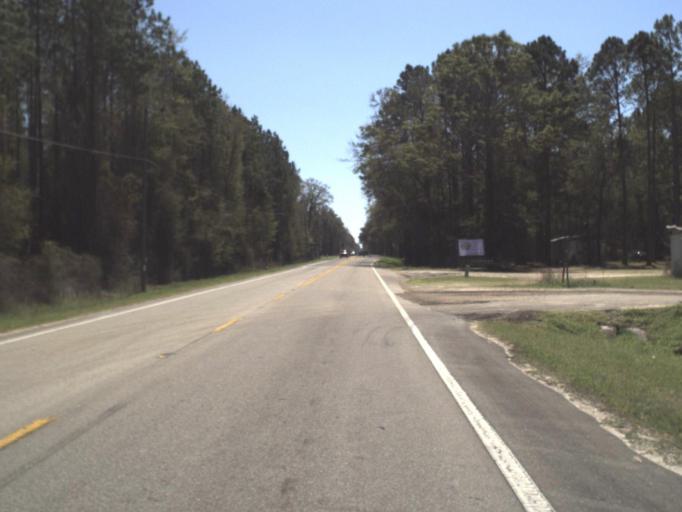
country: US
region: Florida
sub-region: Leon County
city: Woodville
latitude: 30.2725
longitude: -84.2386
